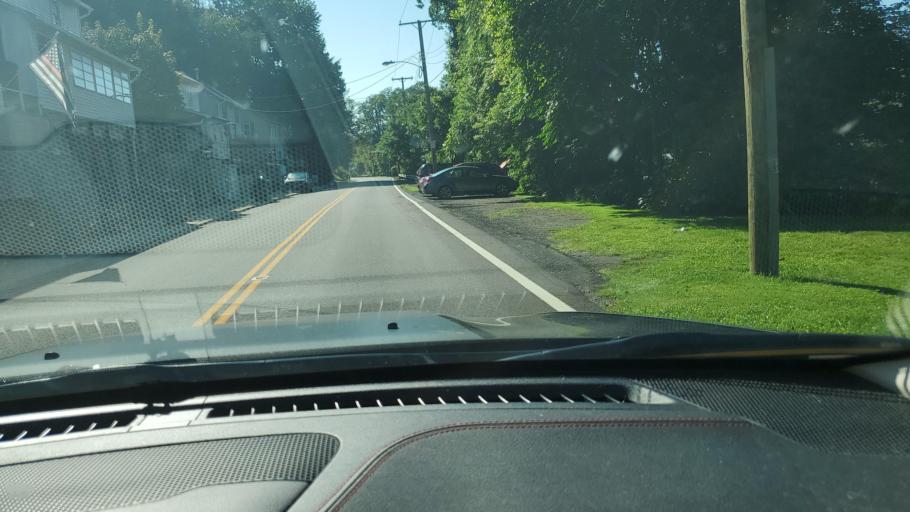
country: US
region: Ohio
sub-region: Mahoning County
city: Lowellville
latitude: 41.0357
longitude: -80.5297
